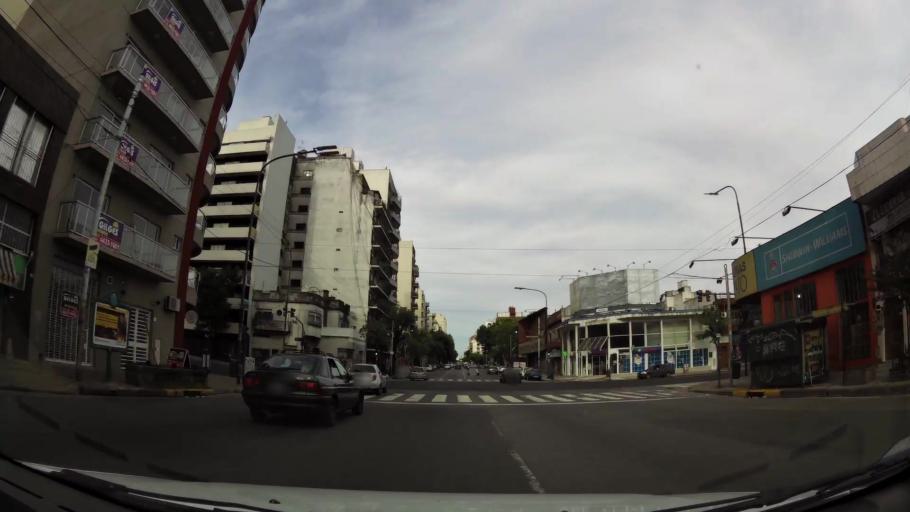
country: AR
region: Buenos Aires F.D.
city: Villa Santa Rita
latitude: -34.6356
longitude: -58.4677
